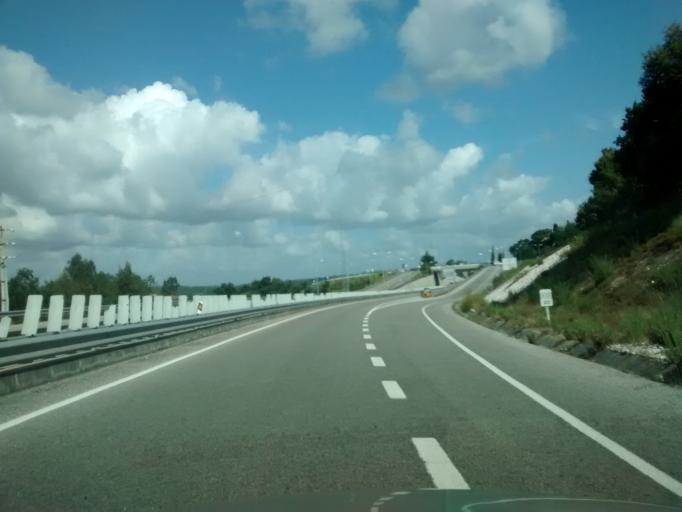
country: PT
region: Aveiro
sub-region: Oliveira do Bairro
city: Oliveira do Bairro
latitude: 40.5114
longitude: -8.4978
